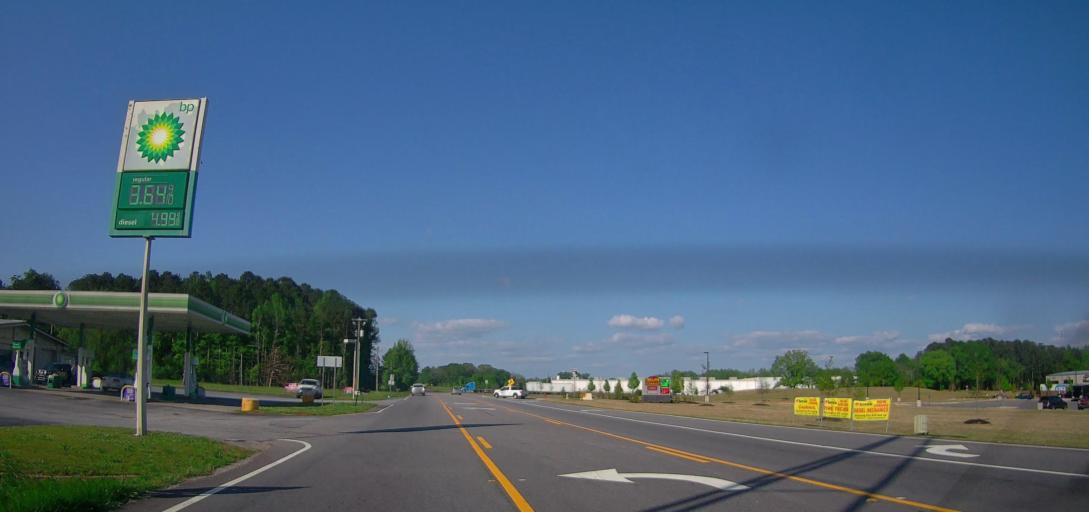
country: US
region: Georgia
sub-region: Morgan County
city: Madison
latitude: 33.5628
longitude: -83.4980
